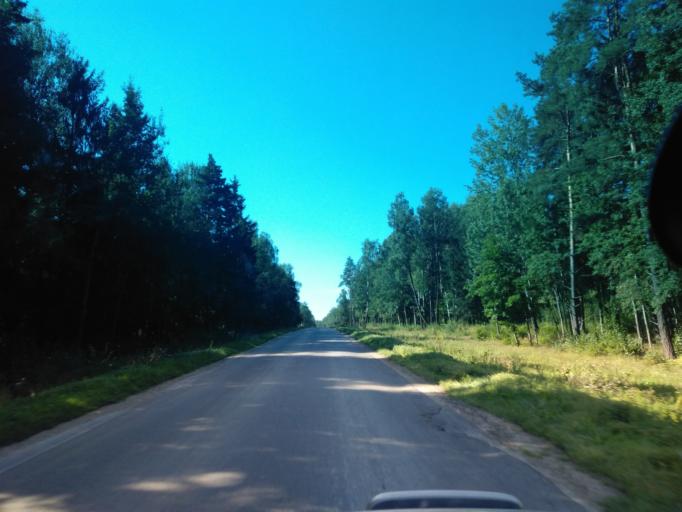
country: BY
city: Fanipol
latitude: 53.7320
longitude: 27.3423
